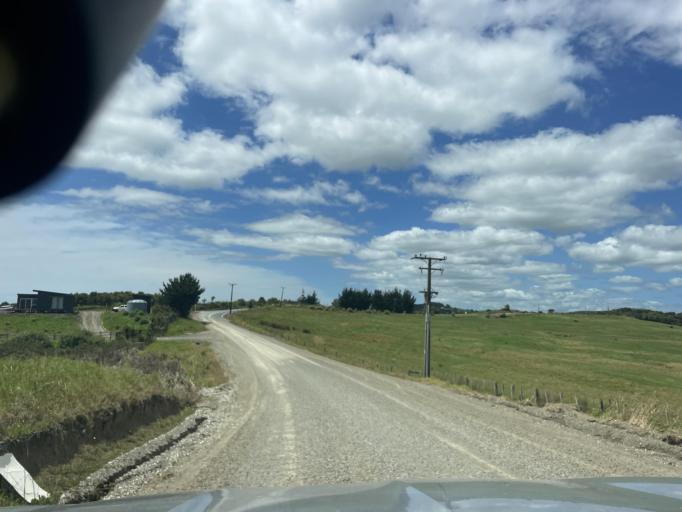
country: NZ
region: Auckland
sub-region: Auckland
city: Wellsford
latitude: -36.1466
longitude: 174.5431
